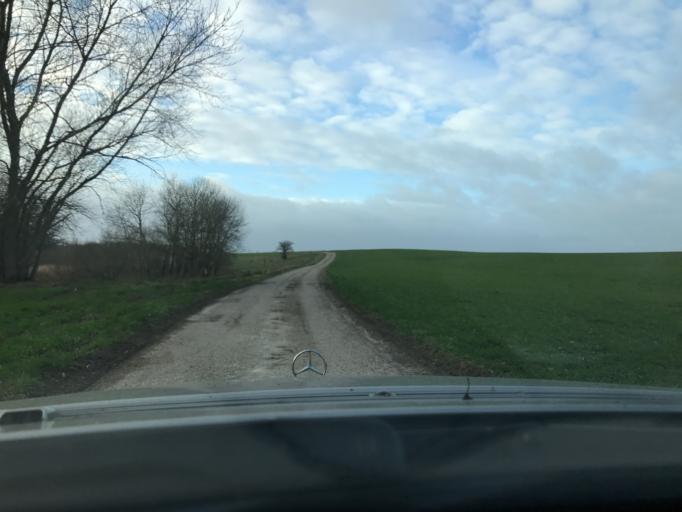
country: DK
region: South Denmark
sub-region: Sonderborg Kommune
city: Nordborg
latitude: 55.0520
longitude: 9.6503
